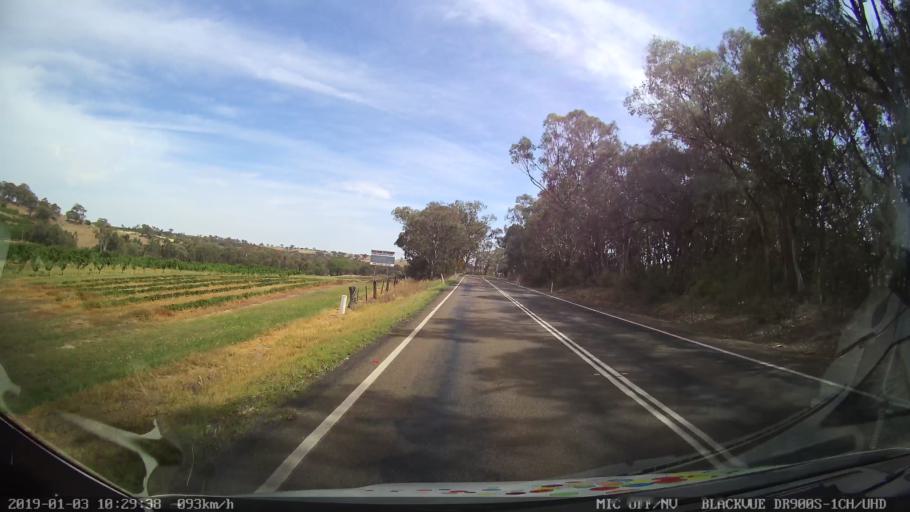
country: AU
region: New South Wales
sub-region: Young
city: Young
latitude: -34.3717
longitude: 148.2616
